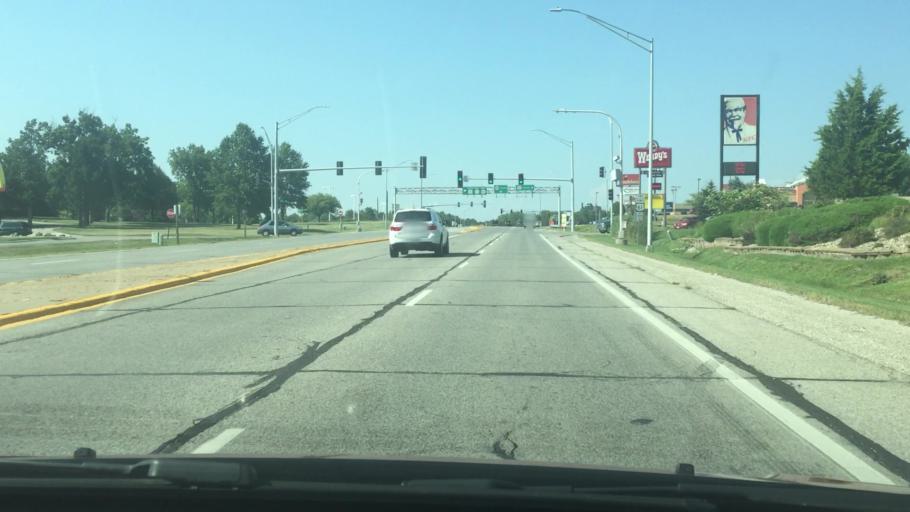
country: US
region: Iowa
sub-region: Muscatine County
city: Muscatine
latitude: 41.4510
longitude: -91.0302
